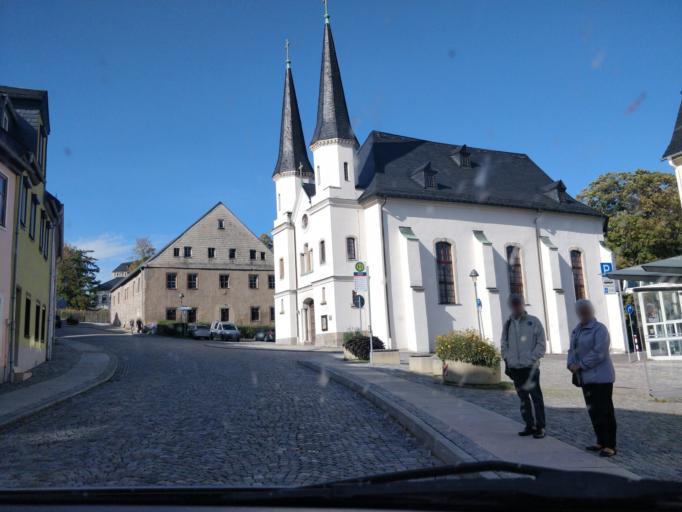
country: DE
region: Saxony
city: Schneeberg
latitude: 50.5965
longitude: 12.6400
